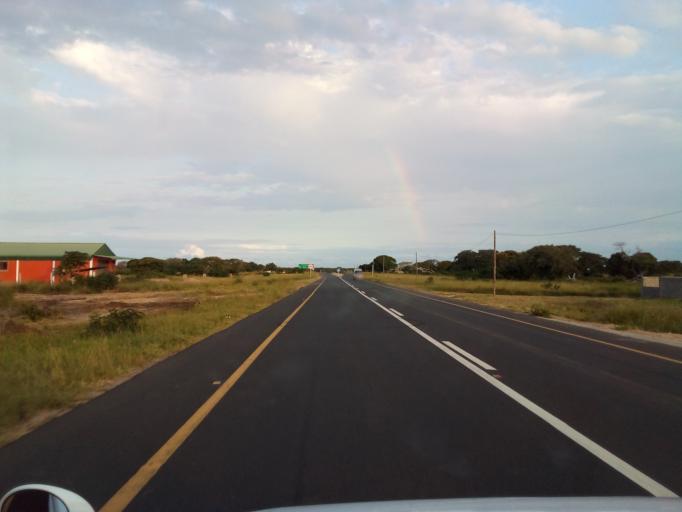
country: MZ
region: Maputo City
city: Maputo
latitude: -26.0767
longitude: 32.6157
